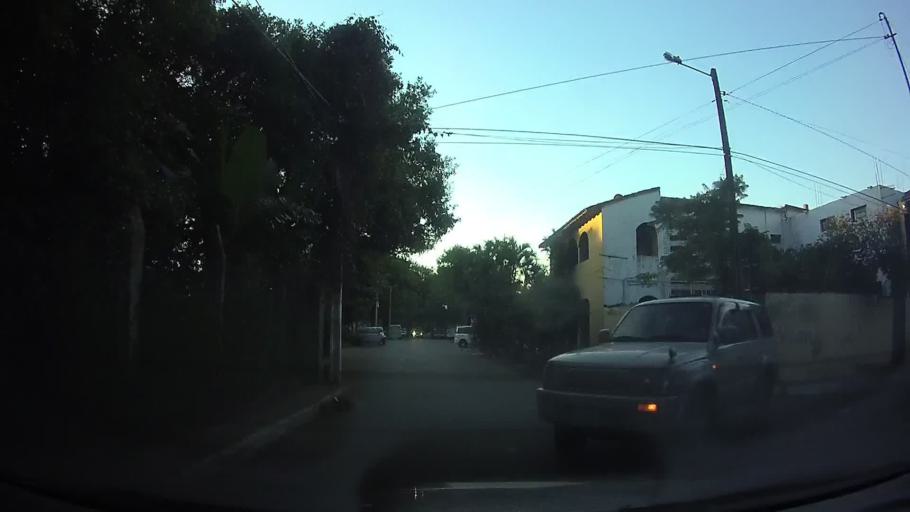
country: PY
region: Central
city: Fernando de la Mora
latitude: -25.3231
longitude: -57.5524
